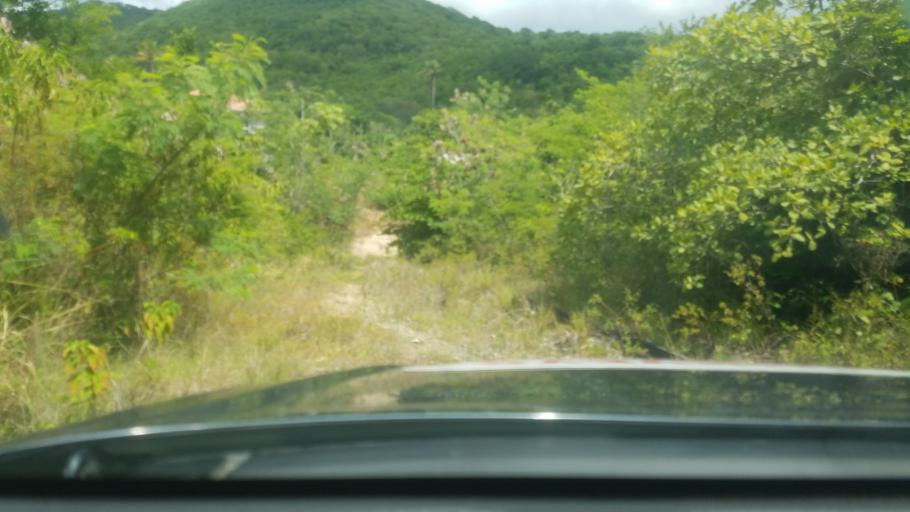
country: LC
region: Praslin
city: Praslin
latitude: 13.8653
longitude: -60.9009
